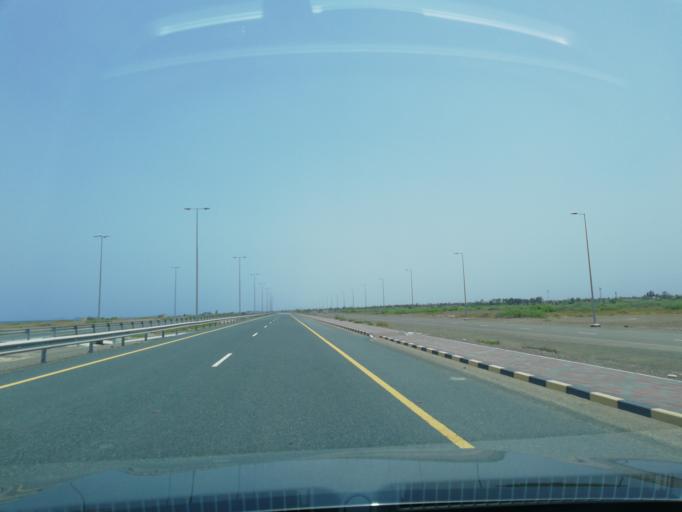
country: OM
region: Al Batinah
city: Shinas
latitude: 24.8530
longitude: 56.4192
